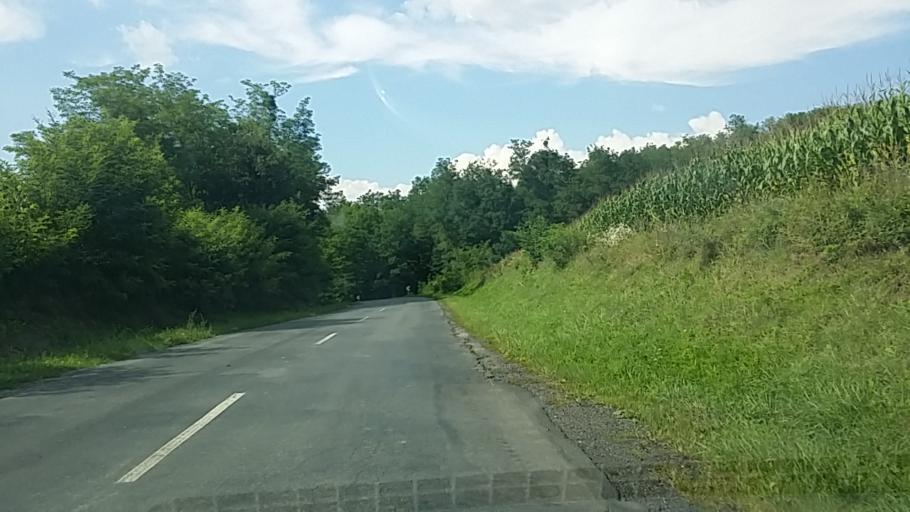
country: HU
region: Zala
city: Becsehely
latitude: 46.5206
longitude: 16.7692
